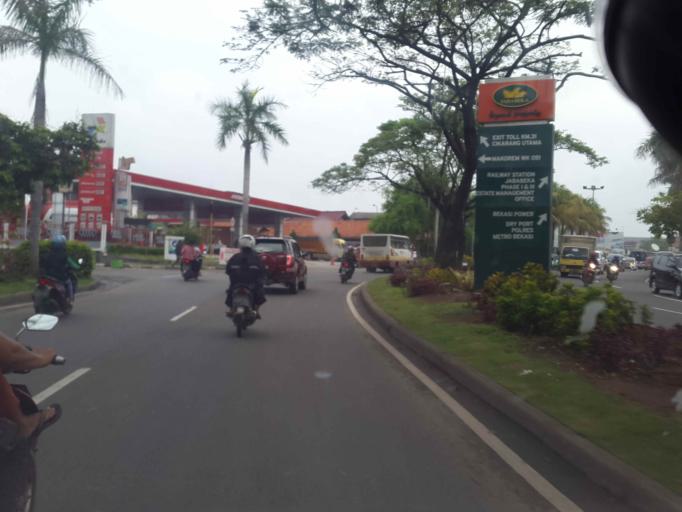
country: ID
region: West Java
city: Cikarang
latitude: -6.2977
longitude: 107.1485
